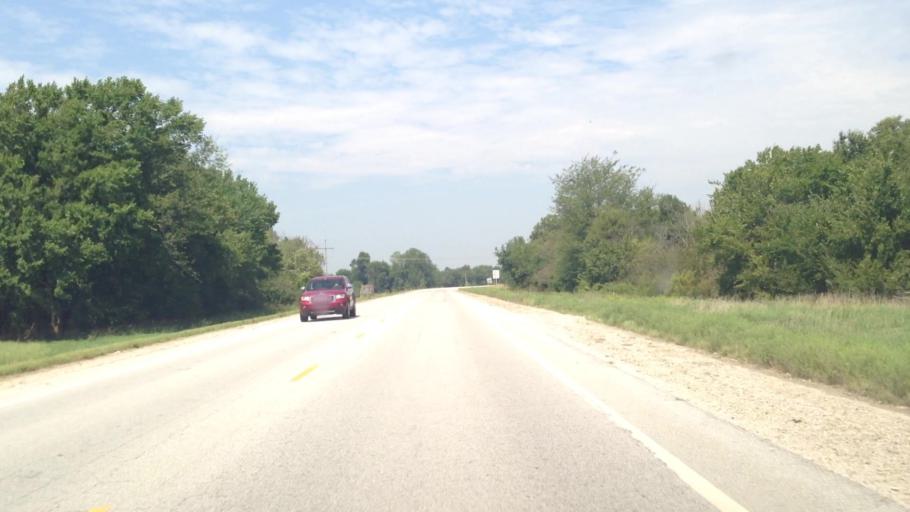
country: US
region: Kansas
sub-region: Labette County
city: Parsons
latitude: 37.3875
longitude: -95.2664
